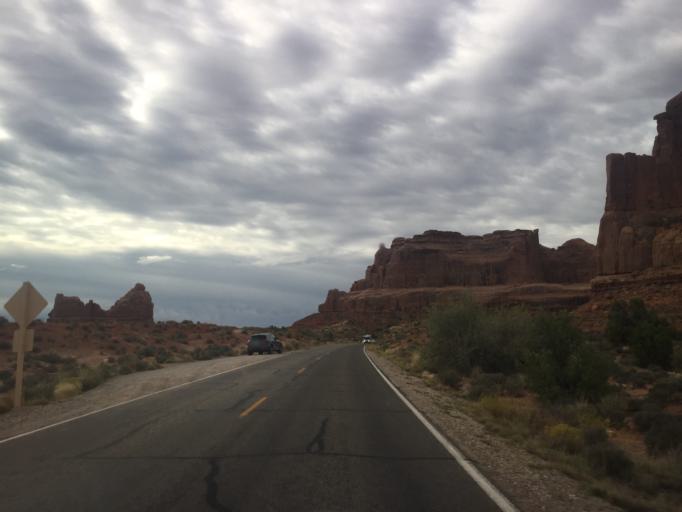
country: US
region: Utah
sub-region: Grand County
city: Moab
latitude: 38.6345
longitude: -109.5987
